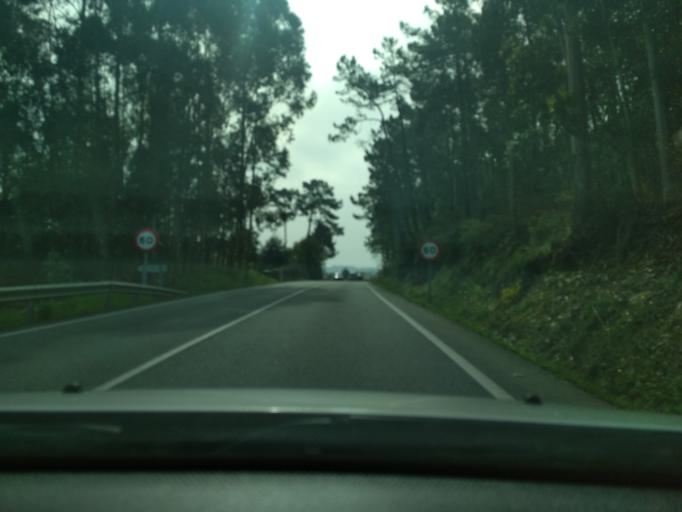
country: ES
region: Galicia
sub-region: Provincia de Pontevedra
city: Catoira
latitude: 42.6760
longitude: -8.7173
